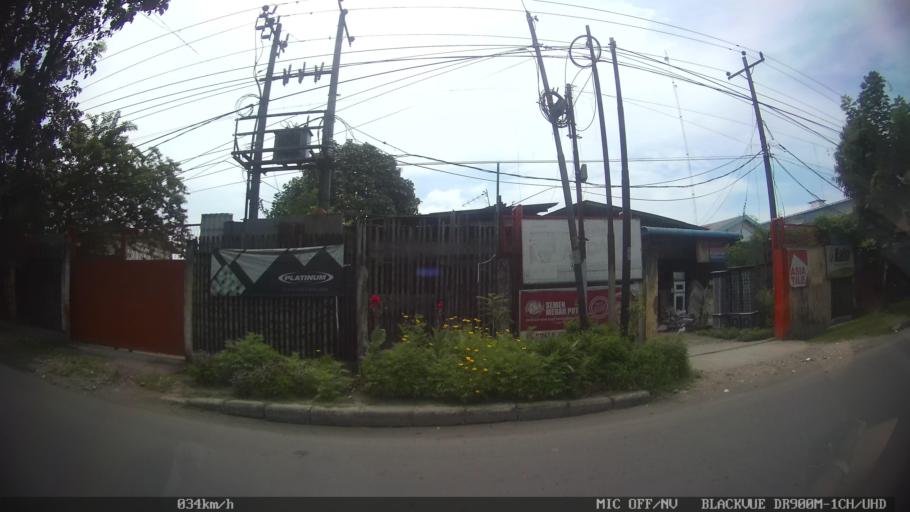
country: ID
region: North Sumatra
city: Labuhan Deli
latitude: 3.6575
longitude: 98.6639
